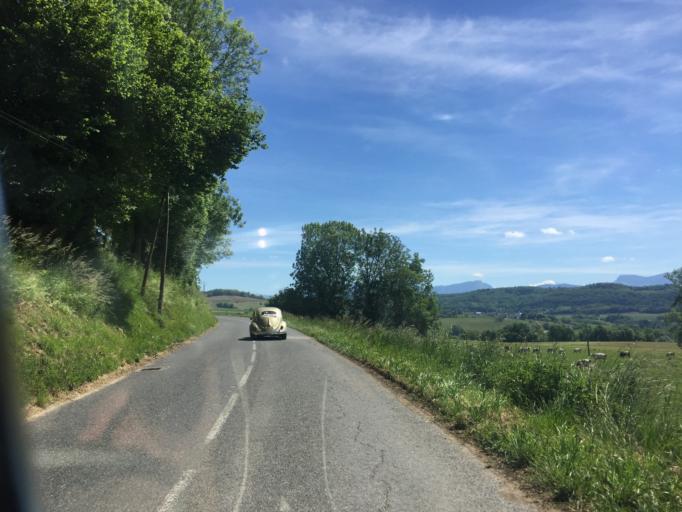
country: FR
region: Rhone-Alpes
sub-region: Departement de la Haute-Savoie
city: Lovagny
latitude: 45.9188
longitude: 5.9970
